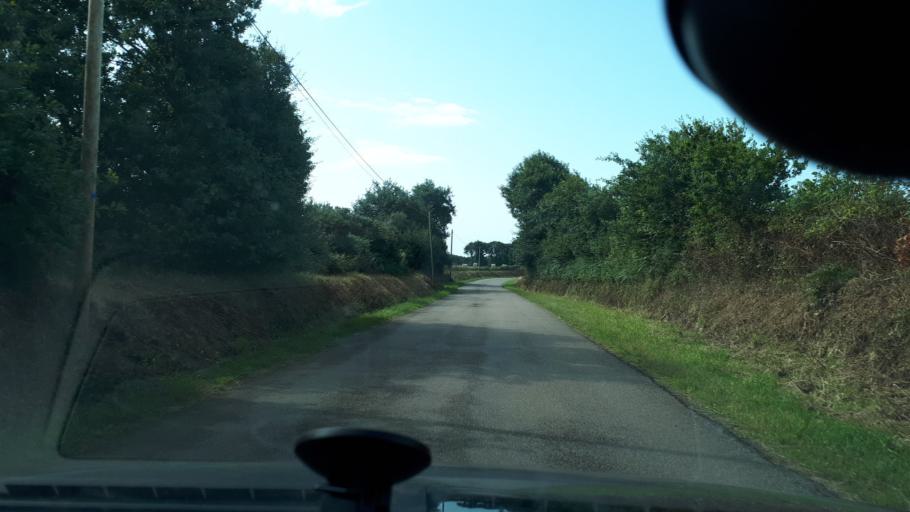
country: FR
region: Brittany
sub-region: Departement du Finistere
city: Landudec
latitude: 47.9955
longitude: -4.3645
